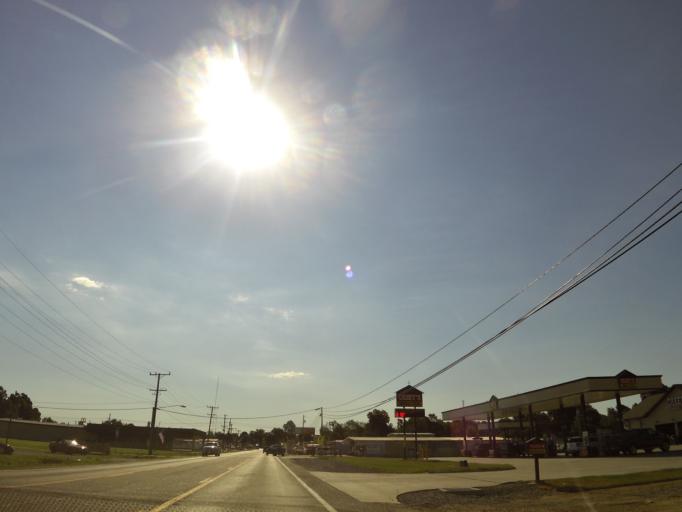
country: US
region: Arkansas
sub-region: Clay County
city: Corning
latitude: 36.4113
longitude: -90.5927
